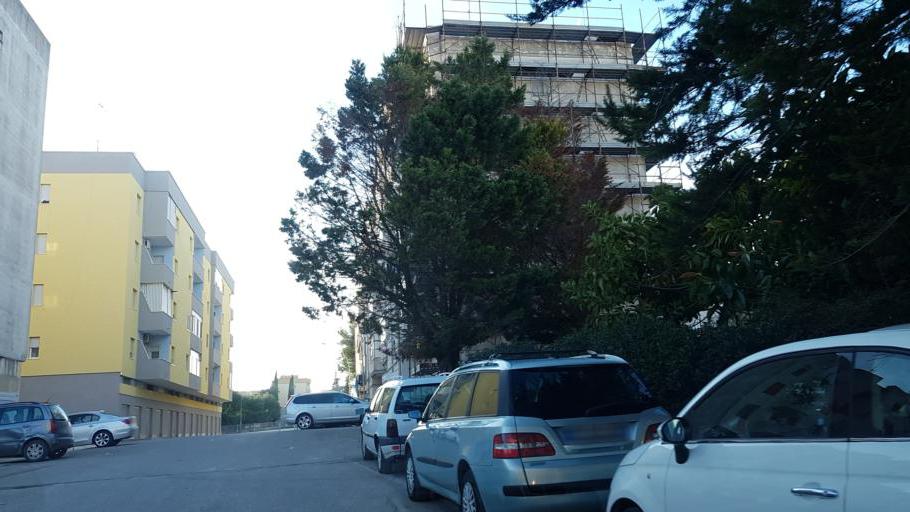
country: IT
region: Apulia
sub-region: Provincia di Brindisi
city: Brindisi
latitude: 40.6183
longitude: 17.9283
